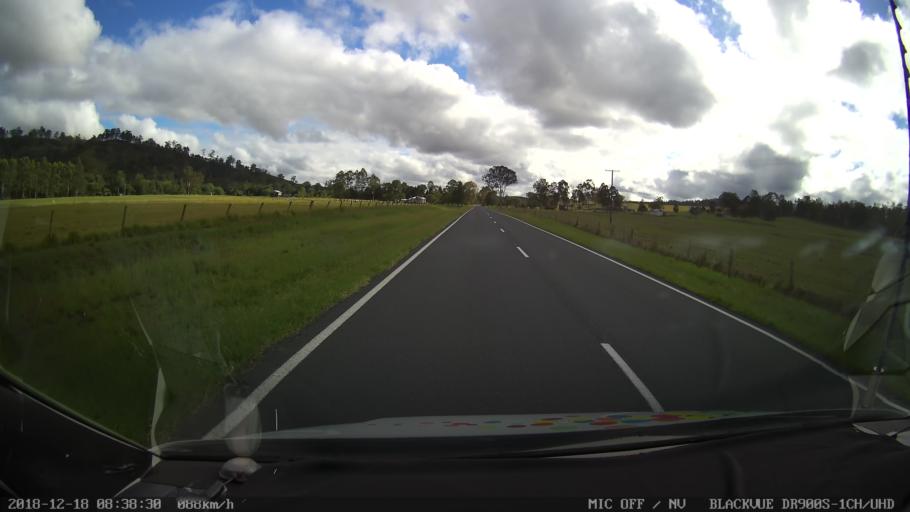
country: AU
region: New South Wales
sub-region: Kyogle
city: Kyogle
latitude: -28.2555
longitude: 152.8282
